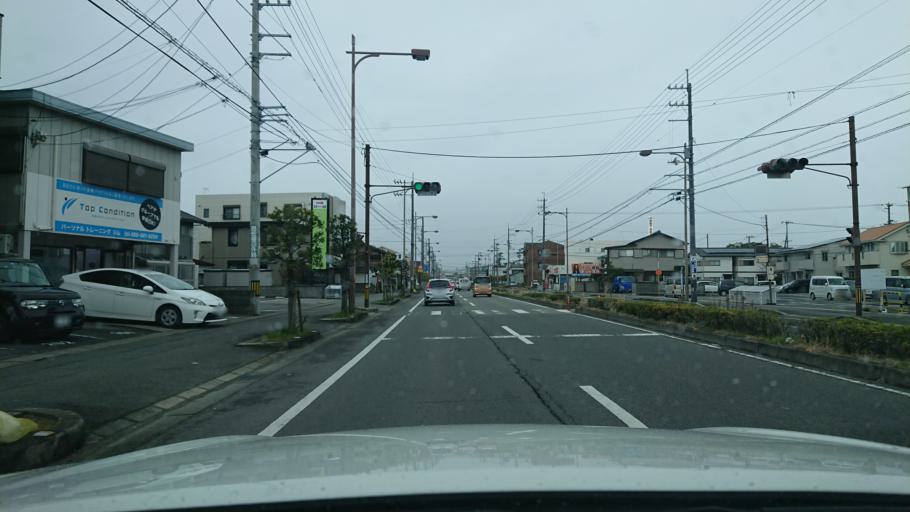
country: JP
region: Tokushima
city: Tokushima-shi
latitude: 34.0866
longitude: 134.5375
